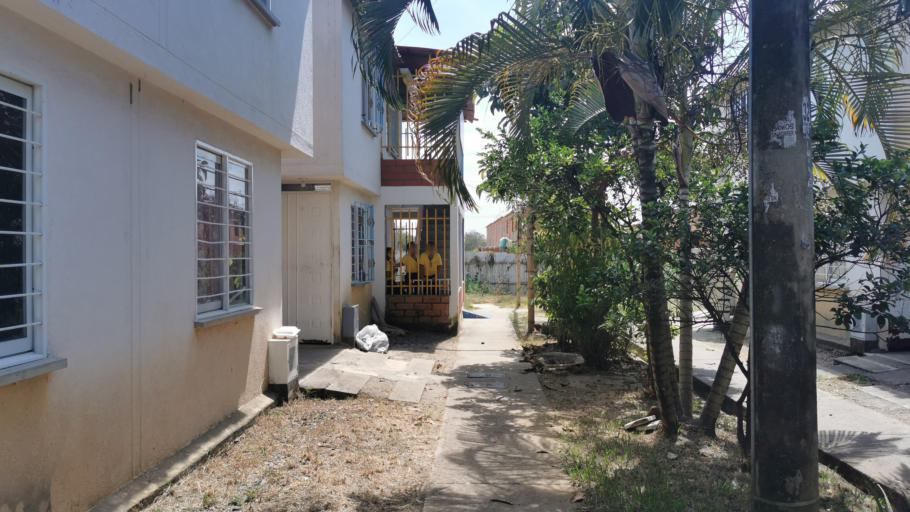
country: CO
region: Valle del Cauca
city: Jamundi
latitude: 3.2428
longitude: -76.5160
